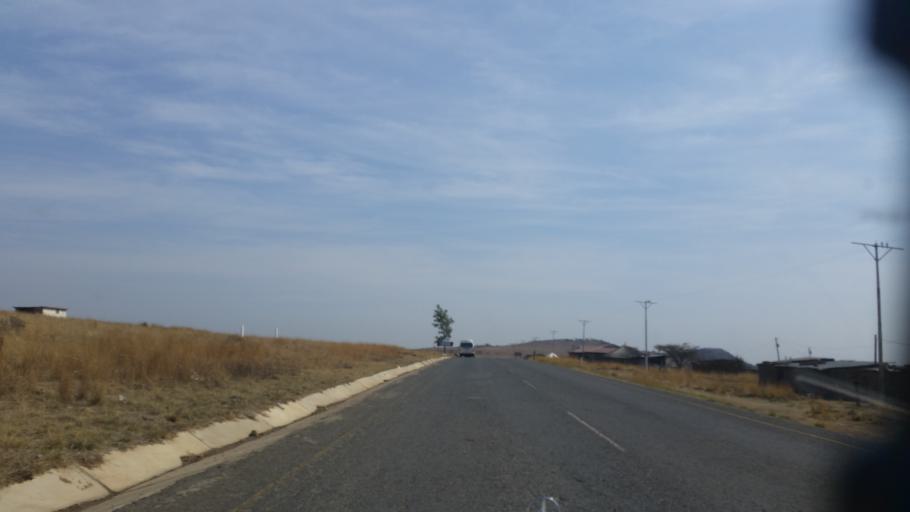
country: ZA
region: KwaZulu-Natal
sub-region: uThukela District Municipality
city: Estcourt
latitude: -29.0455
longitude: 29.9128
